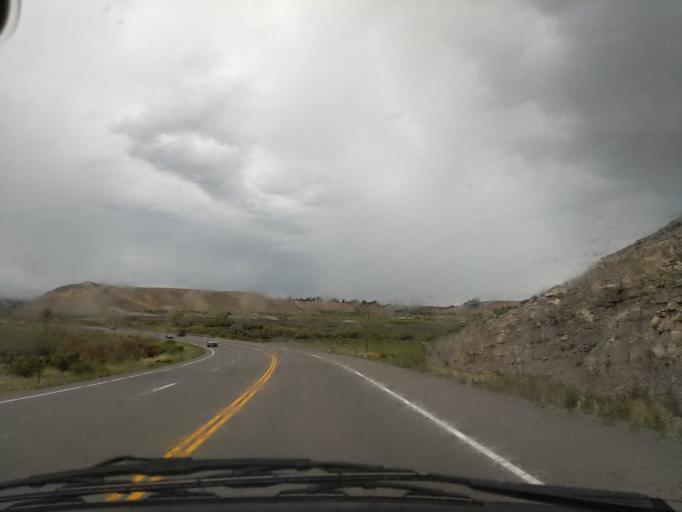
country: US
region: Colorado
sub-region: Delta County
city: Orchard City
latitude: 38.7908
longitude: -107.9385
